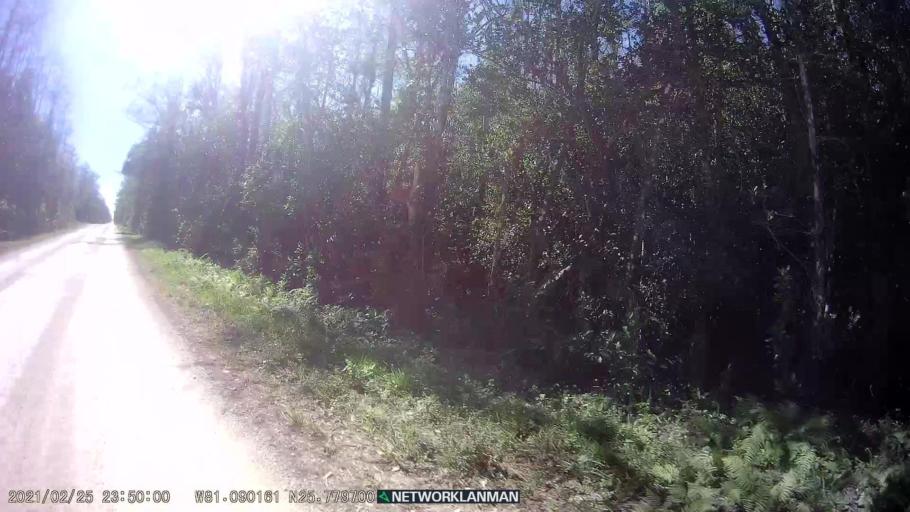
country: US
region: Florida
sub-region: Miami-Dade County
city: The Hammocks
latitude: 25.7796
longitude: -81.0900
